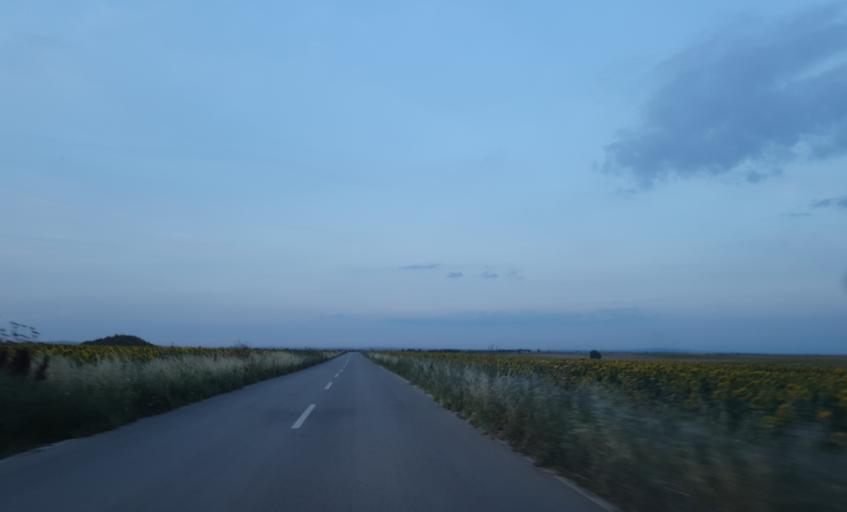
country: TR
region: Tekirdag
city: Beyazkoy
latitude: 41.4253
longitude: 27.6770
